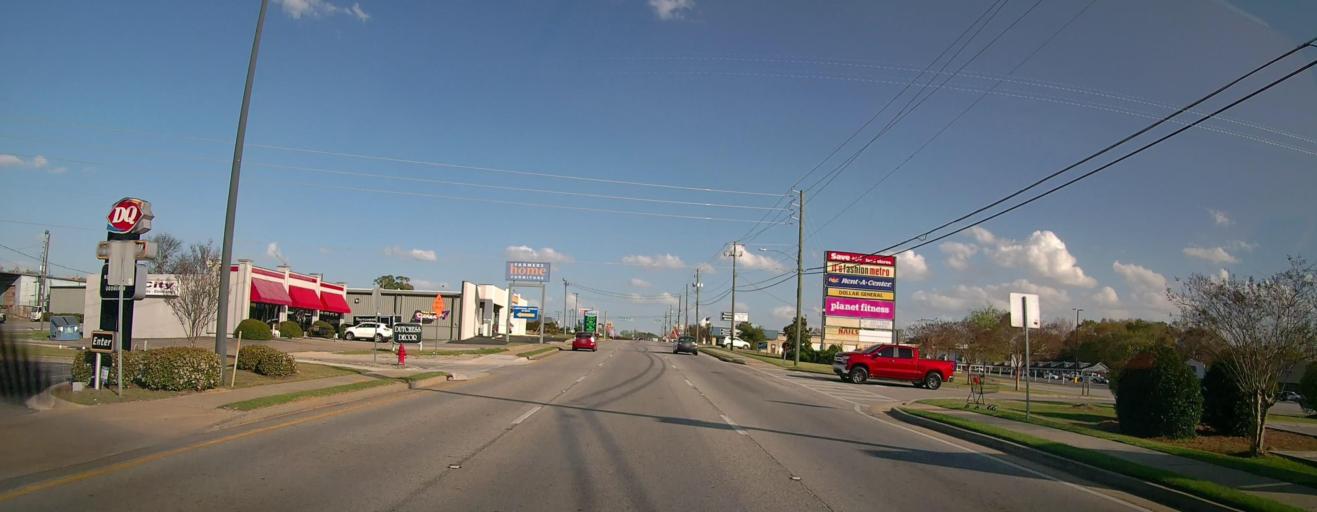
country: US
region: Georgia
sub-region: Toombs County
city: Vidalia
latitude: 32.2150
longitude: -82.4072
